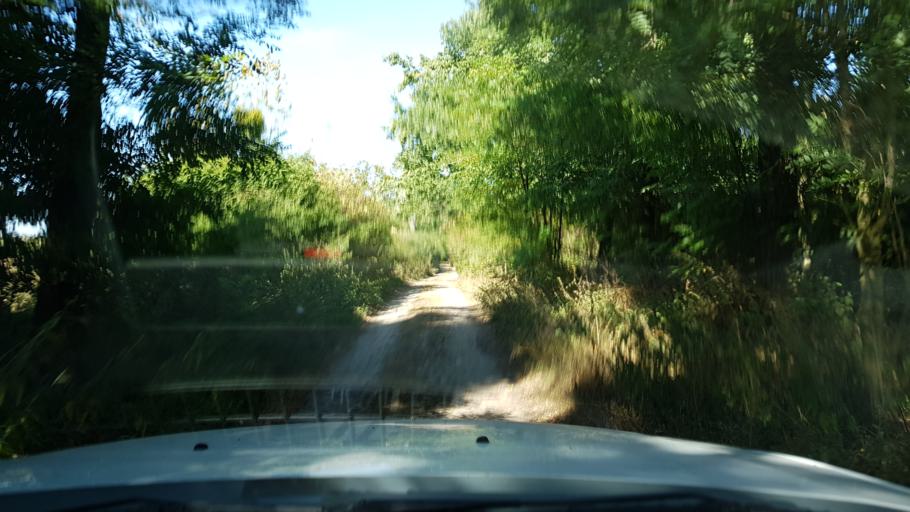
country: PL
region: West Pomeranian Voivodeship
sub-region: Powiat gryfinski
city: Cedynia
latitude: 52.8542
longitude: 14.2267
